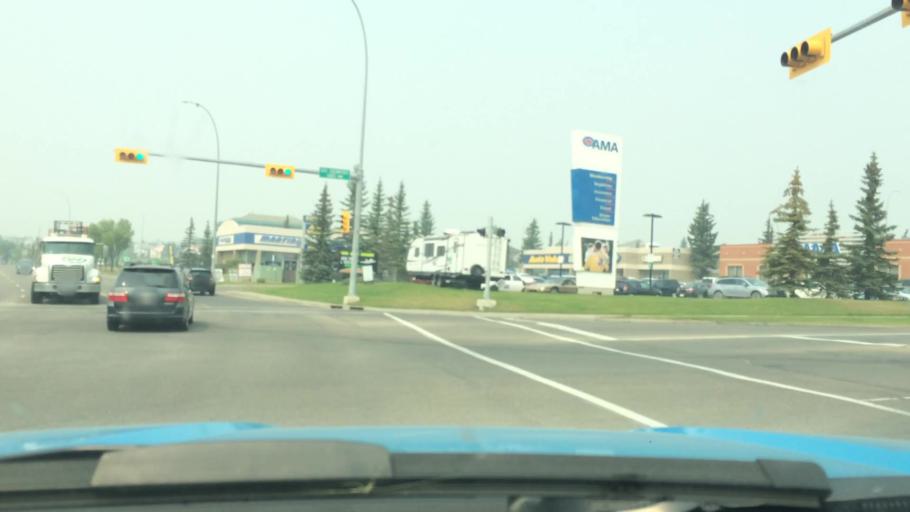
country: CA
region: Alberta
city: Calgary
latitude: 51.1278
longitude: -114.1979
